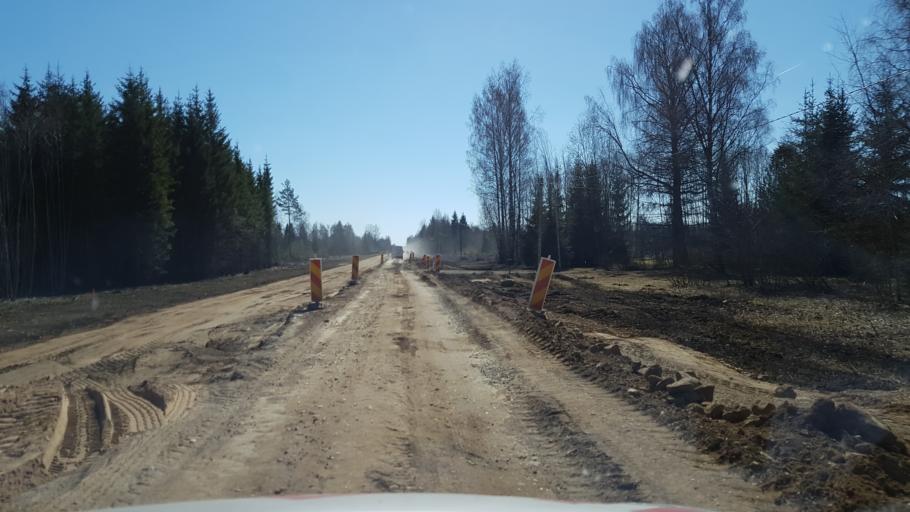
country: EE
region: Jogevamaa
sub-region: Mustvee linn
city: Mustvee
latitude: 59.0349
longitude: 26.6831
